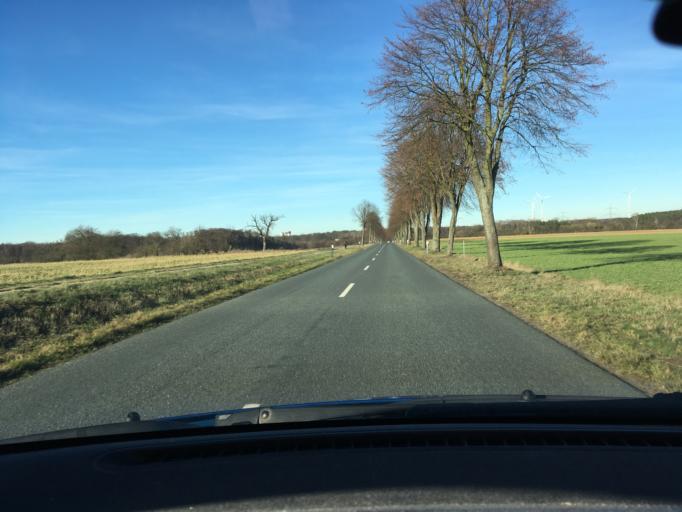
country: DE
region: Lower Saxony
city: Melbeck
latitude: 53.1630
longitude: 10.3832
